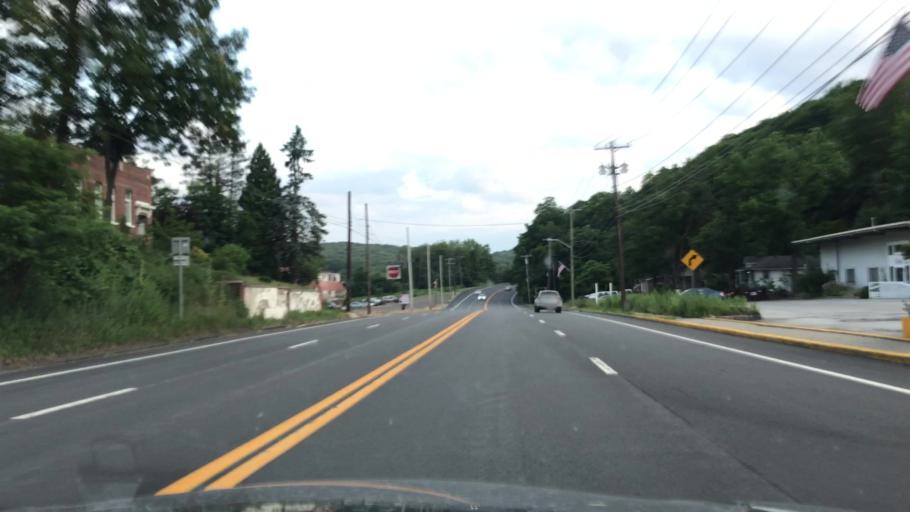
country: US
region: New York
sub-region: Orange County
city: Harriman
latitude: 41.2417
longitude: -74.1766
